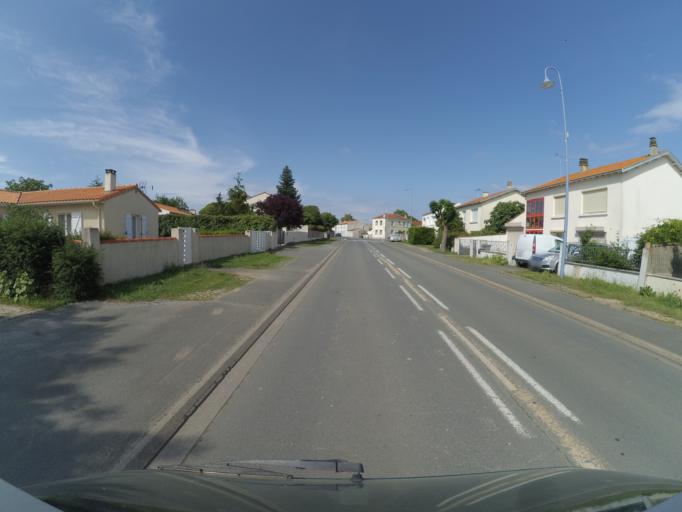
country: FR
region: Poitou-Charentes
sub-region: Departement de la Charente-Maritime
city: Andilly
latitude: 46.2399
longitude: -1.0683
